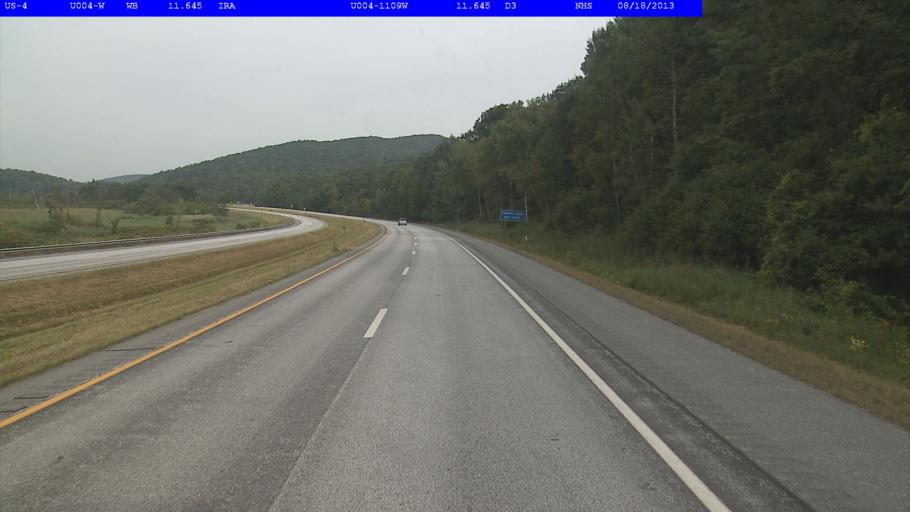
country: US
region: Vermont
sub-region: Rutland County
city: West Rutland
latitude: 43.6117
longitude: -73.0899
